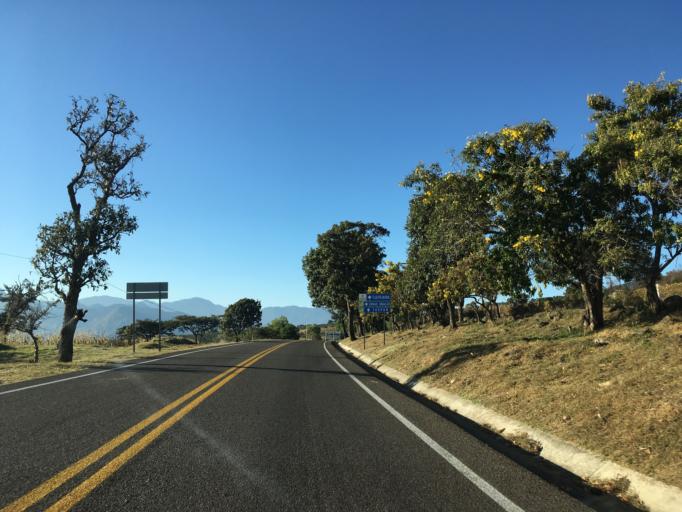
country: MX
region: Michoacan
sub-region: Zitacuaro
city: Puentecillas (Tercera Manzana de Zirahuato)
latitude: 19.4853
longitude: -100.4456
